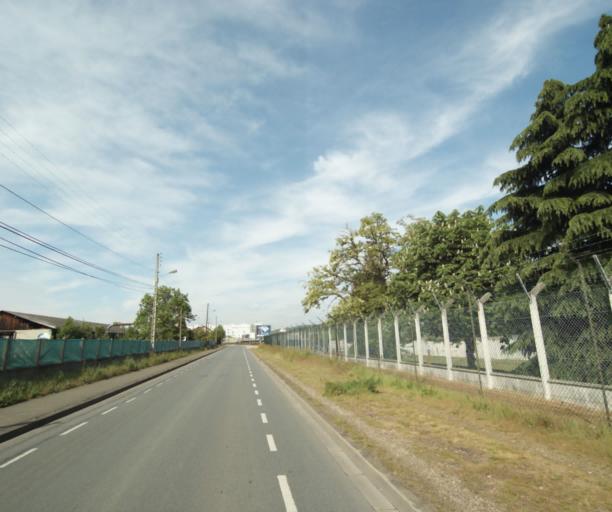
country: FR
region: Ile-de-France
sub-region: Departement des Yvelines
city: Les Mureaux
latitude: 48.9946
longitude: 1.9221
